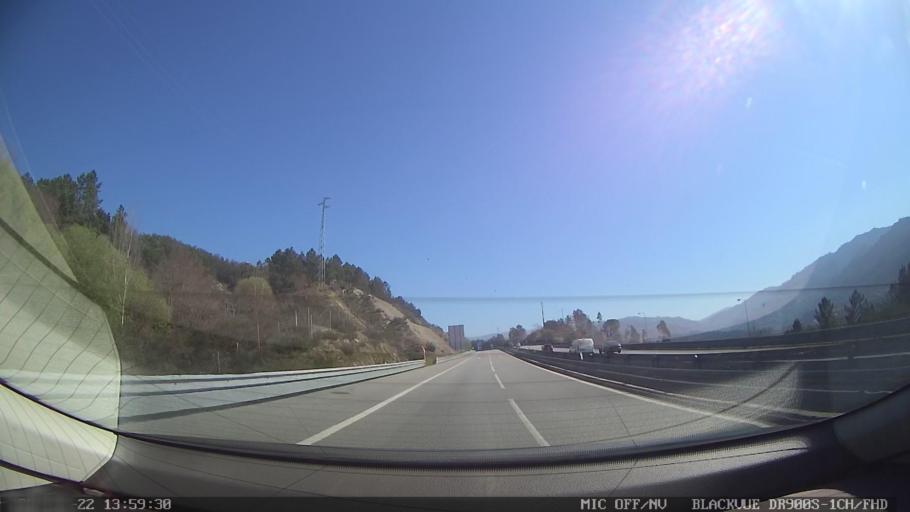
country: PT
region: Porto
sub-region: Amarante
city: Amarante
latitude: 41.2560
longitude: -8.0427
